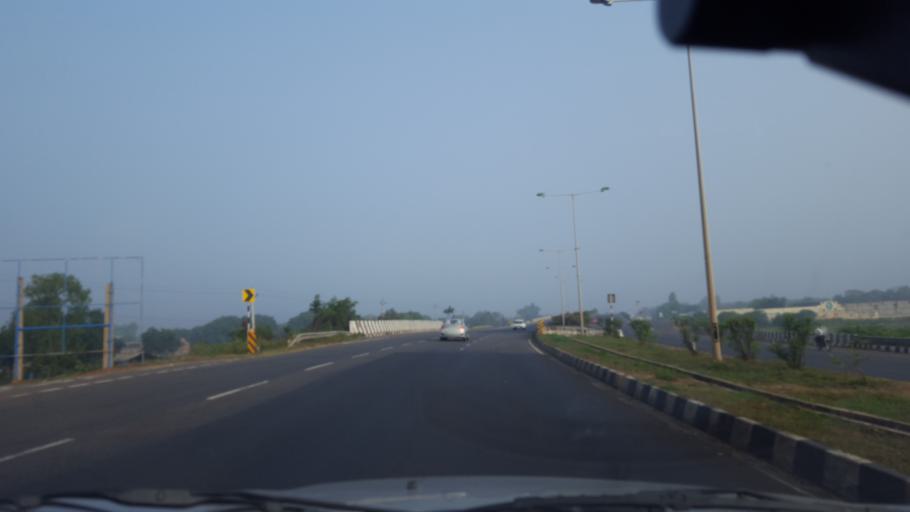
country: IN
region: Andhra Pradesh
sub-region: Prakasam
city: Ongole
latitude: 15.3865
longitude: 80.0396
